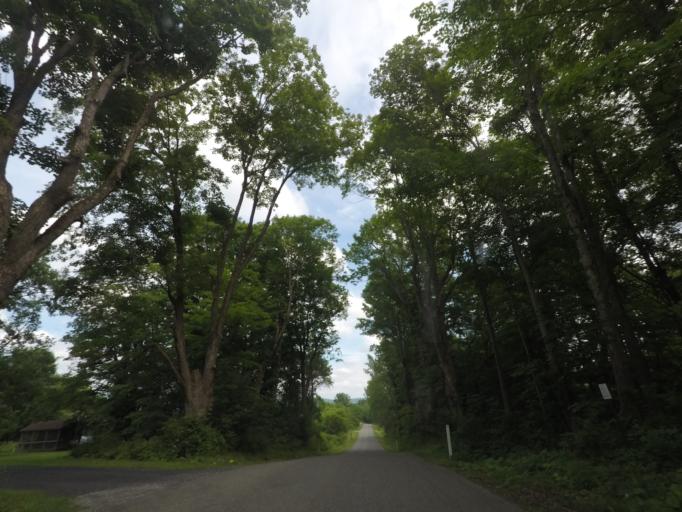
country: US
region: New York
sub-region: Saratoga County
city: Stillwater
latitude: 43.0129
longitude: -73.6456
